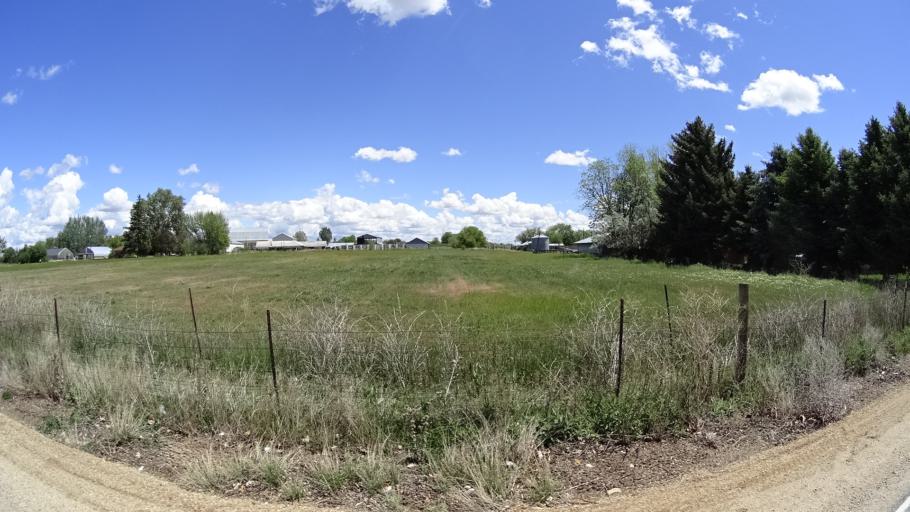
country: US
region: Idaho
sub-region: Ada County
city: Meridian
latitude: 43.5686
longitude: -116.4736
